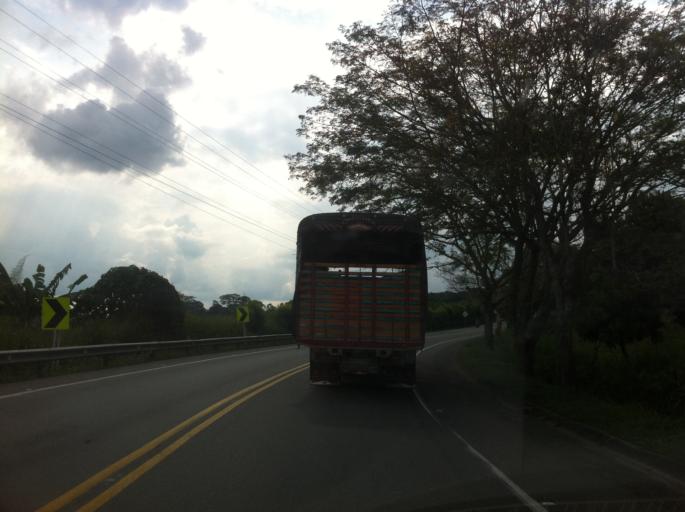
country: CO
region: Quindio
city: La Tebaida
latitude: 4.4485
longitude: -75.8184
